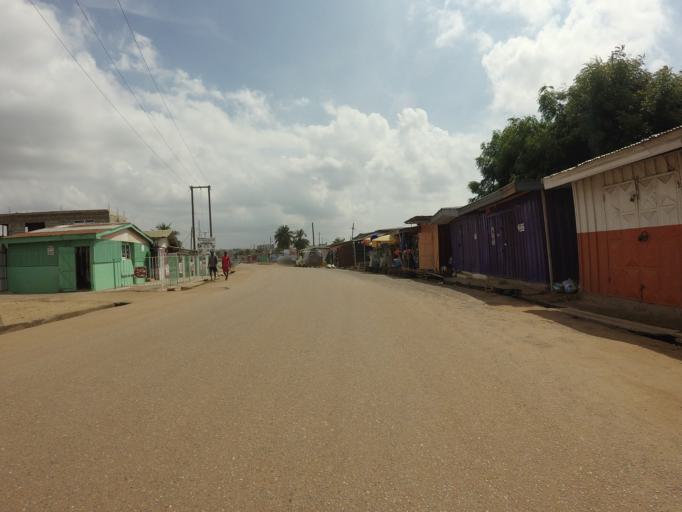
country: GH
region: Greater Accra
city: Nungua
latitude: 5.6091
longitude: -0.0836
